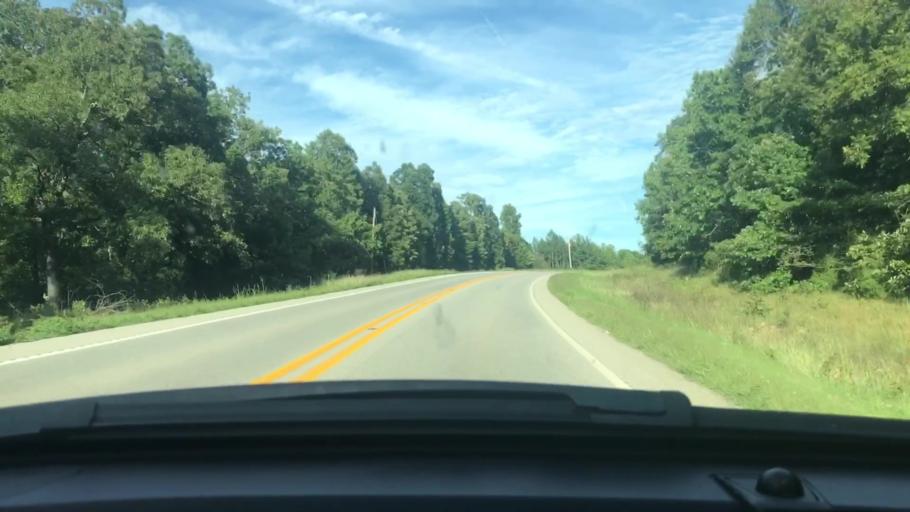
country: US
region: Arkansas
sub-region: Sharp County
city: Cherokee Village
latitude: 36.2767
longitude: -91.3139
